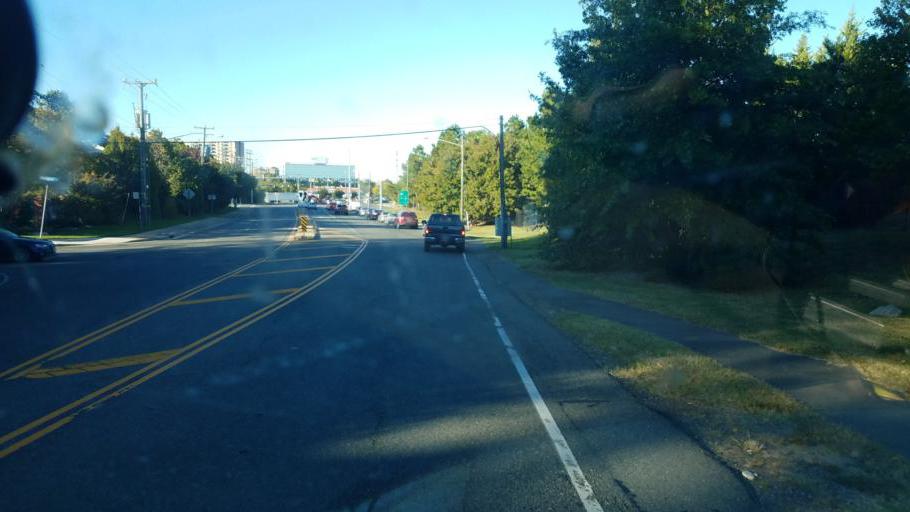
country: US
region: Virginia
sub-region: Fairfax County
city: Belle Haven
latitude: 38.7883
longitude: -77.0608
